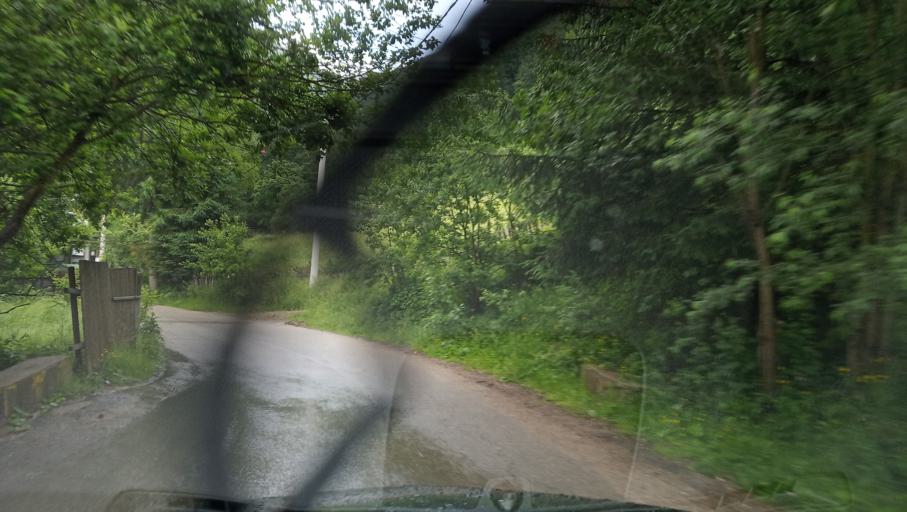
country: RO
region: Hunedoara
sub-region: Oras Petrila
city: Petrila
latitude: 45.3928
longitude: 23.4452
